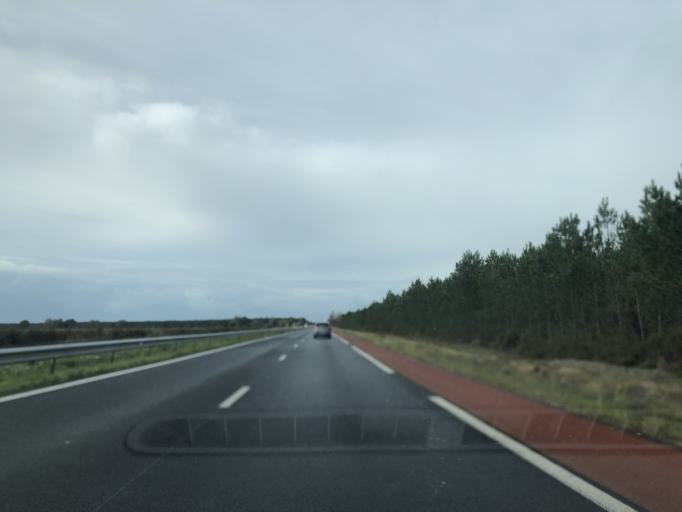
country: FR
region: Aquitaine
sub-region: Departement de la Gironde
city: Lanton
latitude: 44.7787
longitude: -1.0079
